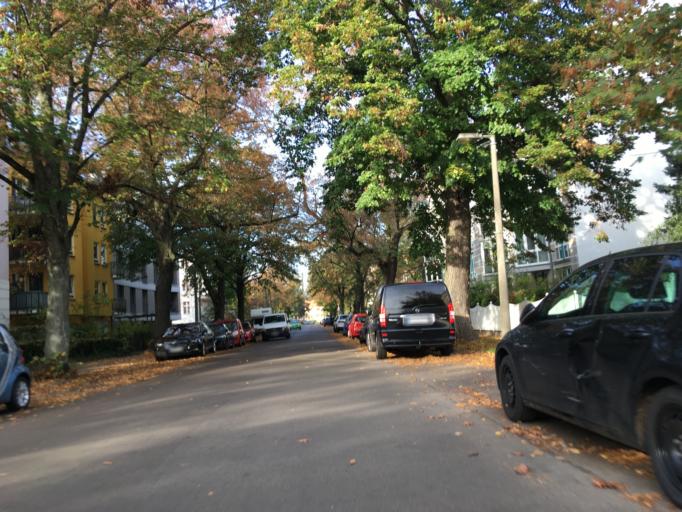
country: DE
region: Berlin
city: Niederschonhausen
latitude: 52.5862
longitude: 13.3975
